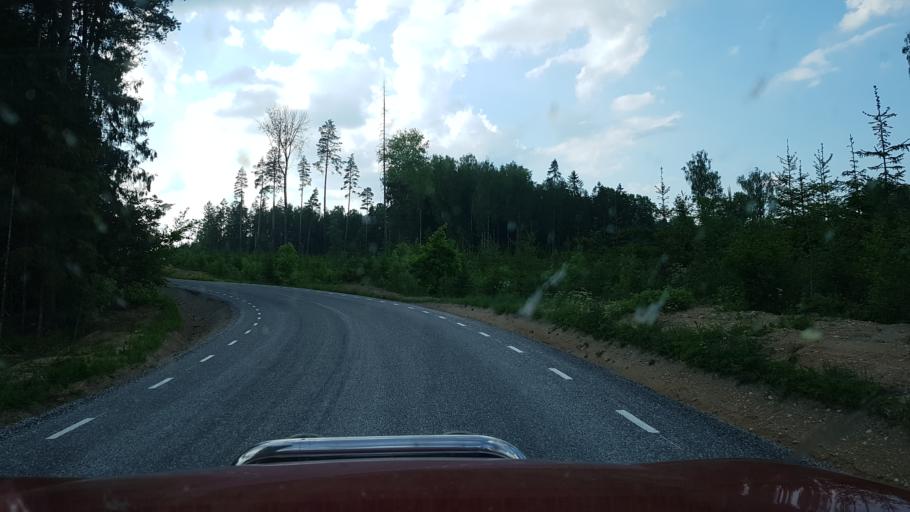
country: EE
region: Tartu
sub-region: UElenurme vald
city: Ulenurme
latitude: 58.0959
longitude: 26.8042
